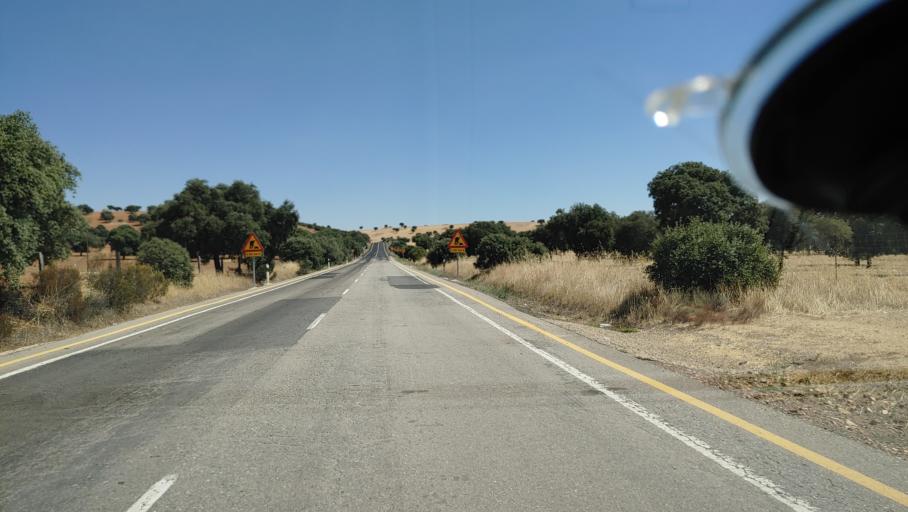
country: ES
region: Castille-La Mancha
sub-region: Provincia de Ciudad Real
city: Saceruela
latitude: 39.0158
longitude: -4.4716
